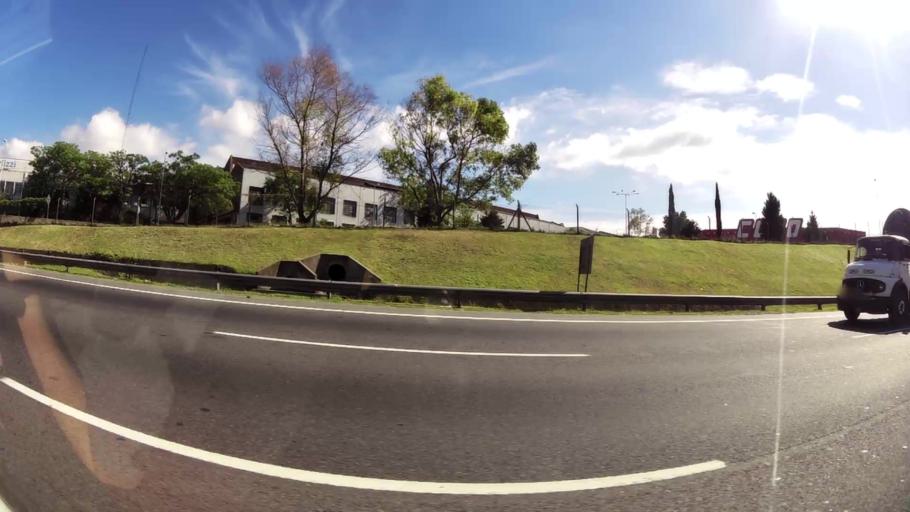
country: AR
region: Buenos Aires
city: Caseros
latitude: -34.6299
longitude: -58.5507
